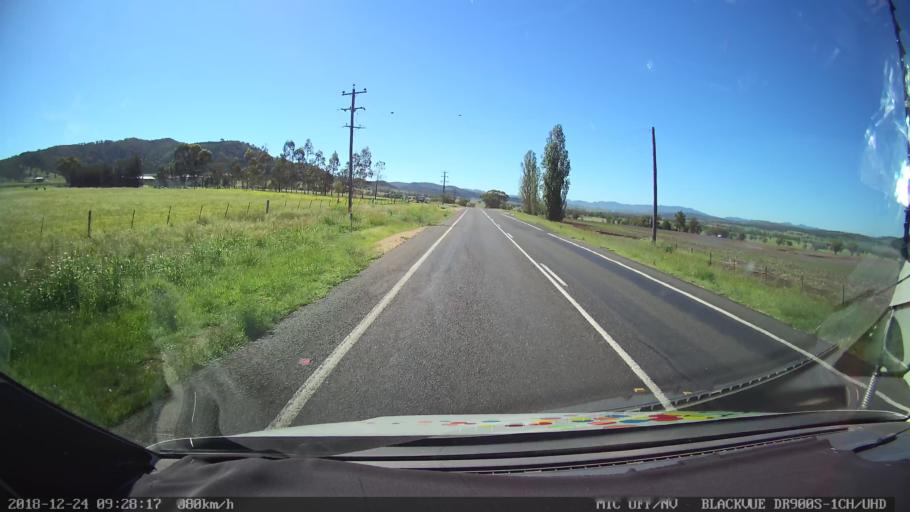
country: AU
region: New South Wales
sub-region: Liverpool Plains
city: Quirindi
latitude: -31.5362
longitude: 150.6875
